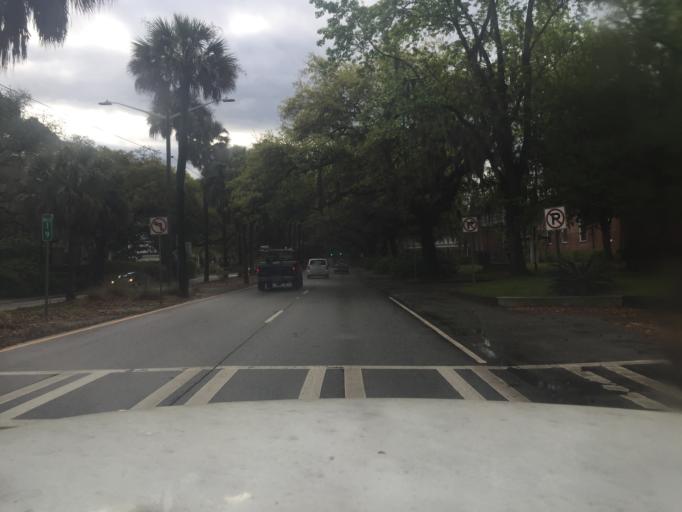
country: US
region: Georgia
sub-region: Chatham County
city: Savannah
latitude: 32.0499
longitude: -81.0917
